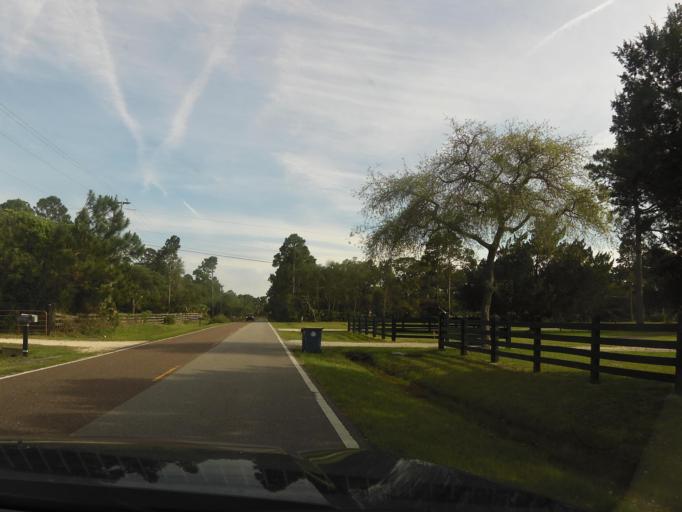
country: US
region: Florida
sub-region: Duval County
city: Atlantic Beach
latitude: 30.4772
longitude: -81.4703
